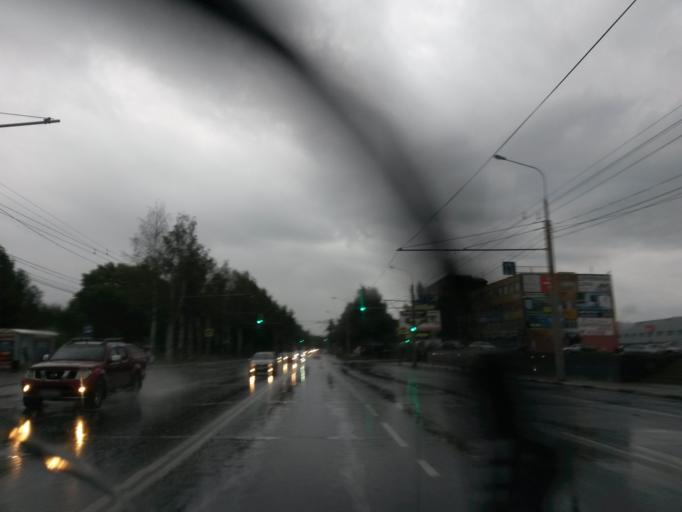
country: RU
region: Jaroslavl
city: Yaroslavl
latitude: 57.6554
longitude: 39.8687
